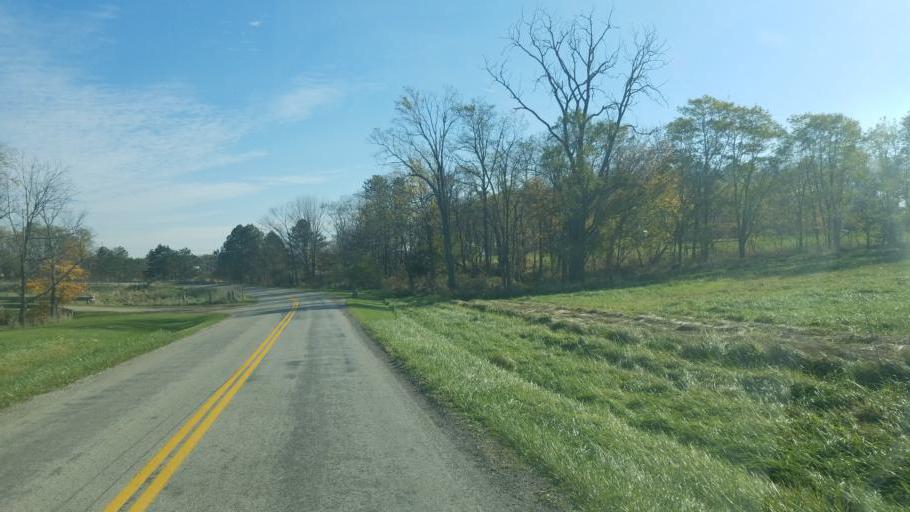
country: US
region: Ohio
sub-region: Ashland County
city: Ashland
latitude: 40.8289
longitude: -82.3227
